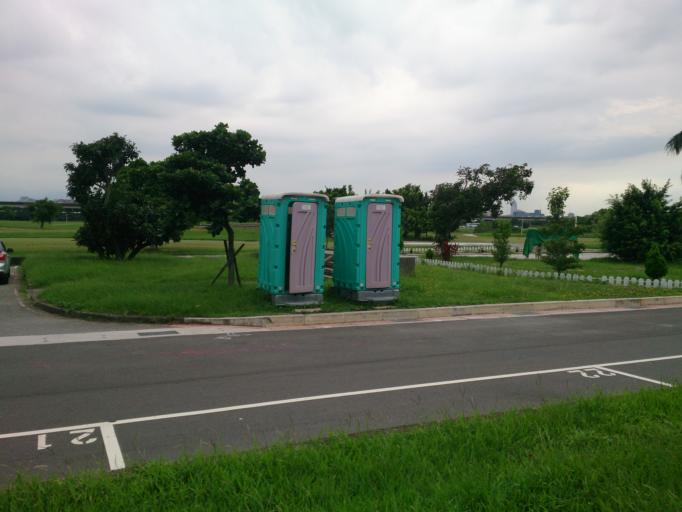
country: TW
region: Taipei
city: Taipei
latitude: 25.0763
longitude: 121.5604
